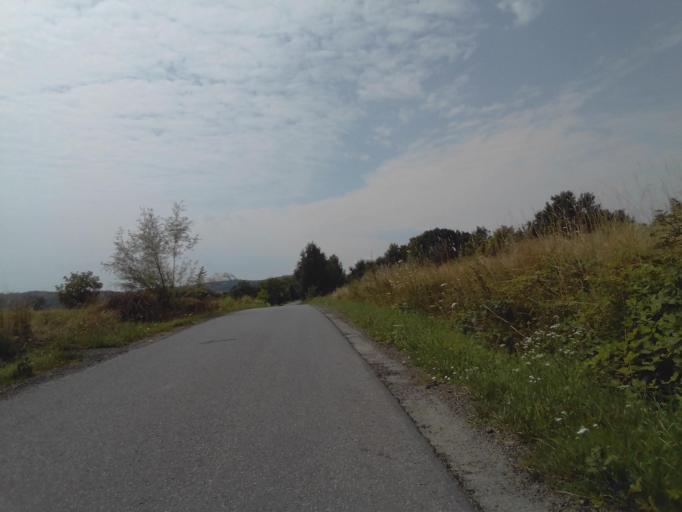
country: PL
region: Subcarpathian Voivodeship
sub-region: Powiat jasielski
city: Jaslo
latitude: 49.8089
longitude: 21.5076
